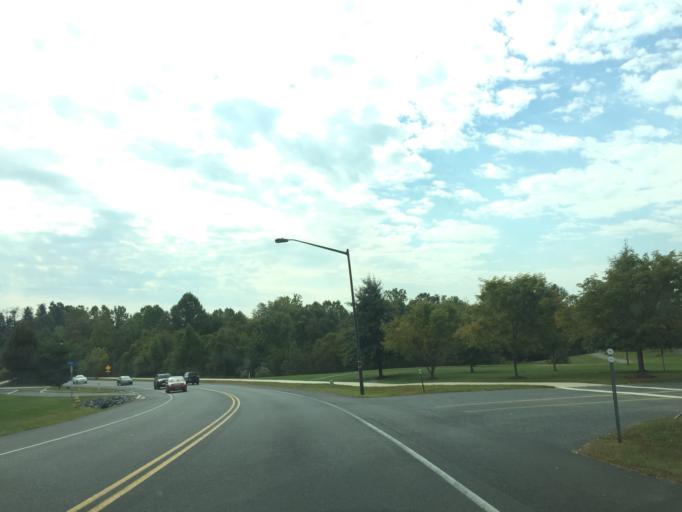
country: US
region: Maryland
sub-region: Harford County
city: Bel Air South
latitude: 39.4850
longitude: -76.3284
